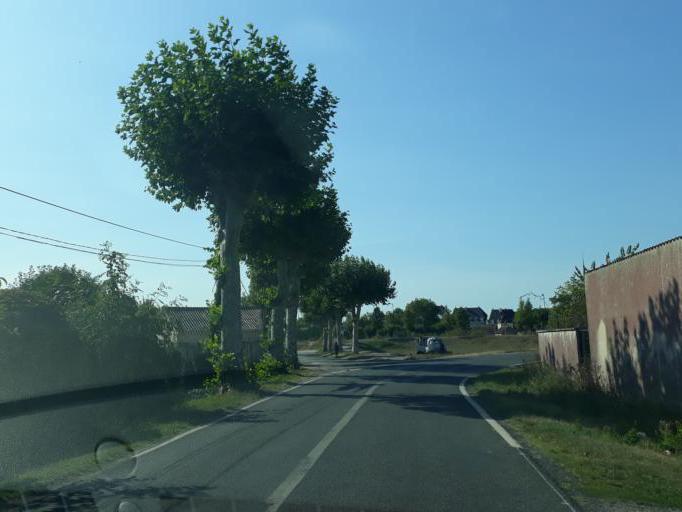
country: FR
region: Centre
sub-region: Departement du Loir-et-Cher
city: Selles-sur-Cher
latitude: 47.2723
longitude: 1.5603
